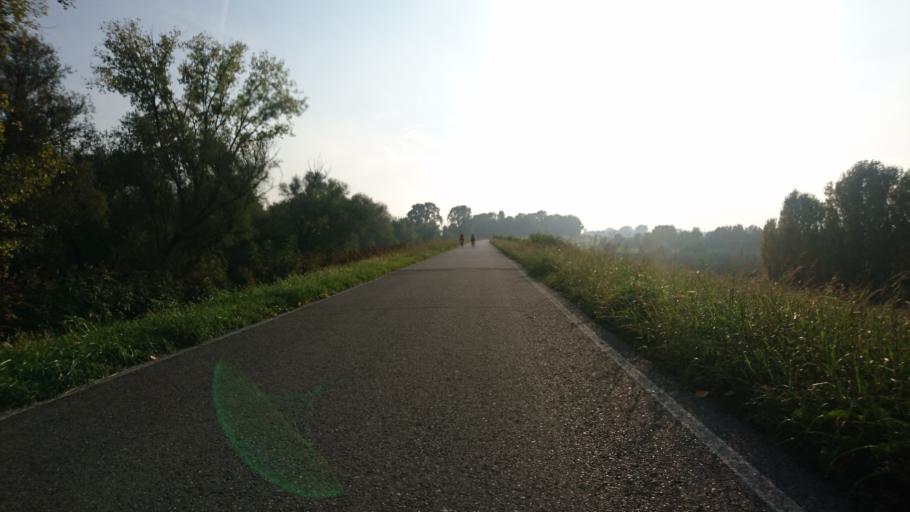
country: IT
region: Emilia-Romagna
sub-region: Provincia di Ferrara
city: Francolino
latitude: 44.9127
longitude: 11.6623
